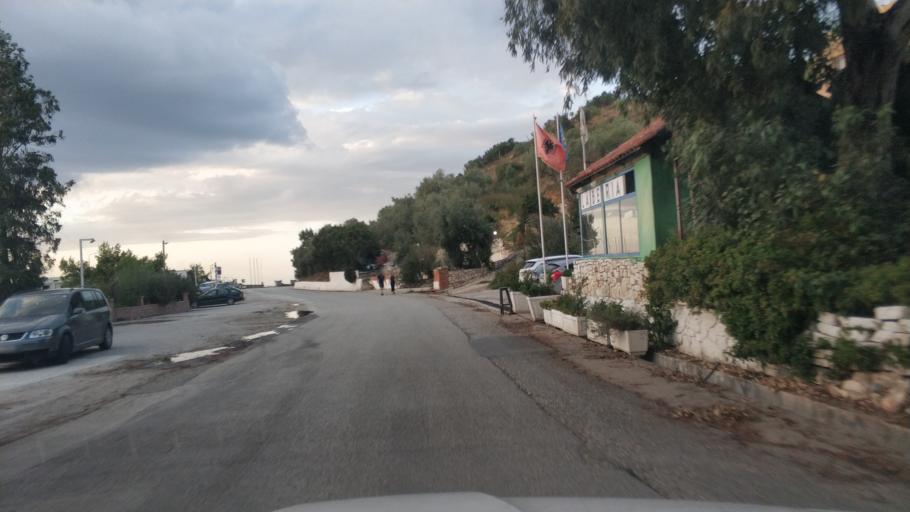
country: AL
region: Vlore
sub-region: Rrethi i Vlores
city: Orikum
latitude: 40.3609
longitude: 19.4809
